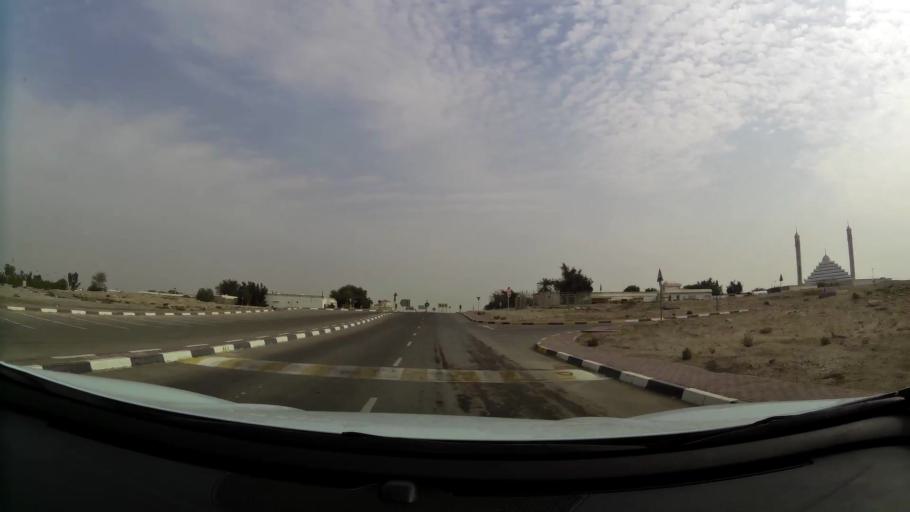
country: AE
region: Abu Dhabi
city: Abu Dhabi
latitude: 24.6842
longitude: 54.7673
